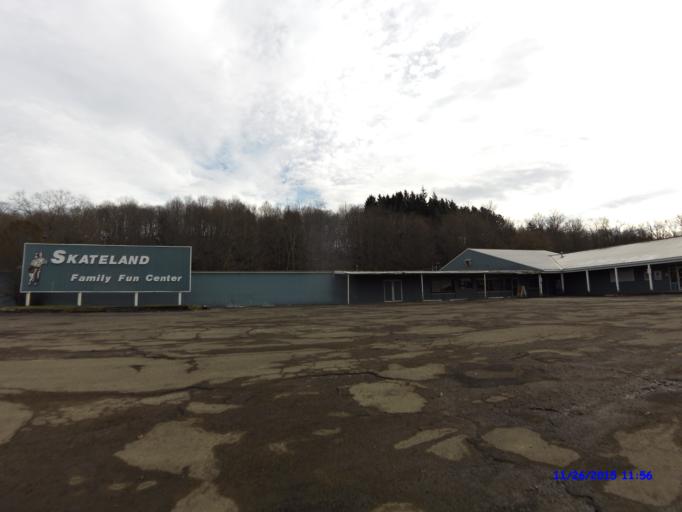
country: US
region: New York
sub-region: Cattaraugus County
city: Franklinville
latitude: 42.3304
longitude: -78.4601
